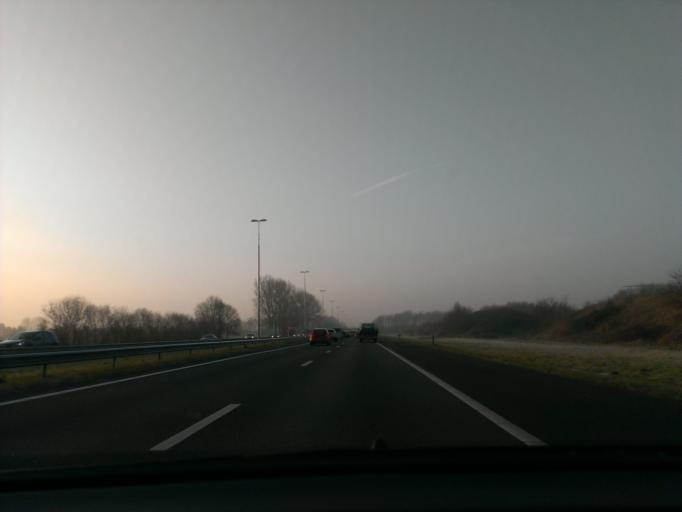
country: NL
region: Gelderland
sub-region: Gemeente Apeldoorn
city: Apeldoorn
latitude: 52.2402
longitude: 6.0110
